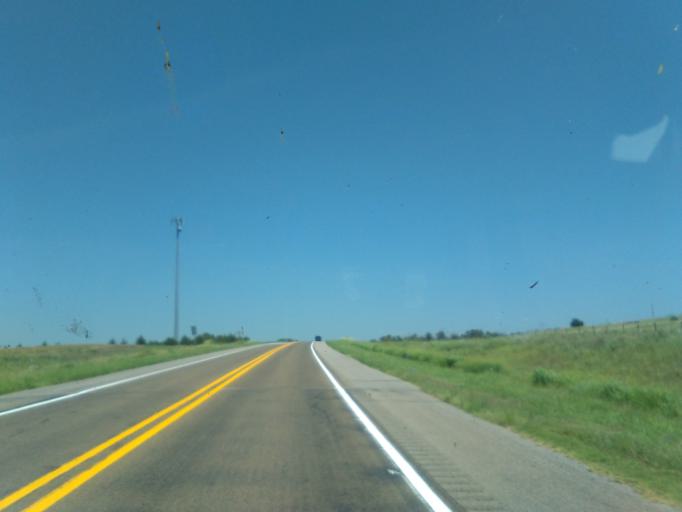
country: US
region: Nebraska
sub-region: Lincoln County
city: North Platte
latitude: 40.7484
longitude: -100.7246
